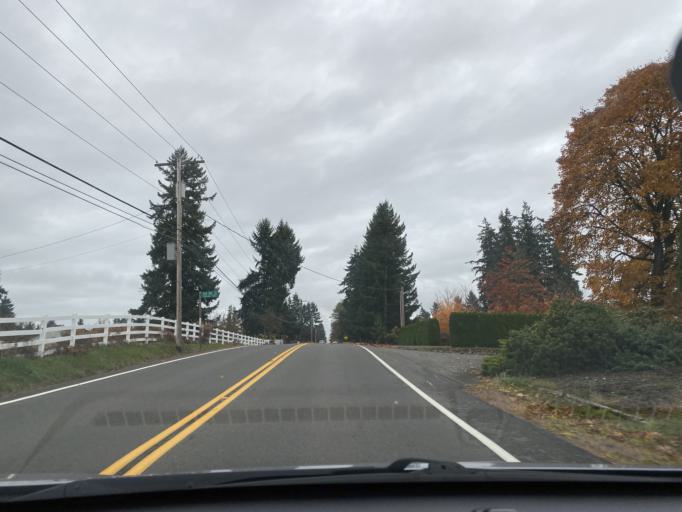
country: US
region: Washington
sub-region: King County
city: Lake Morton-Berrydale
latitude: 47.3005
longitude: -122.1322
